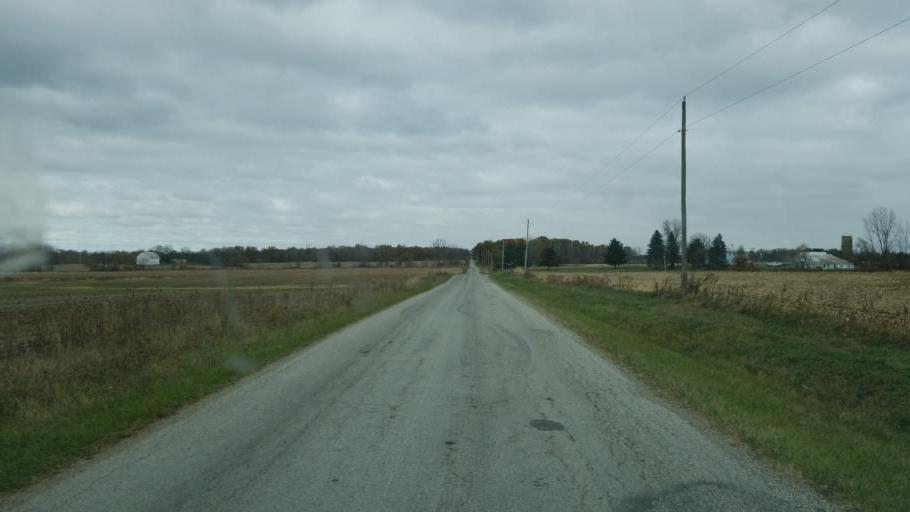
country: US
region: Ohio
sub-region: Crawford County
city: Galion
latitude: 40.6708
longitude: -82.7468
